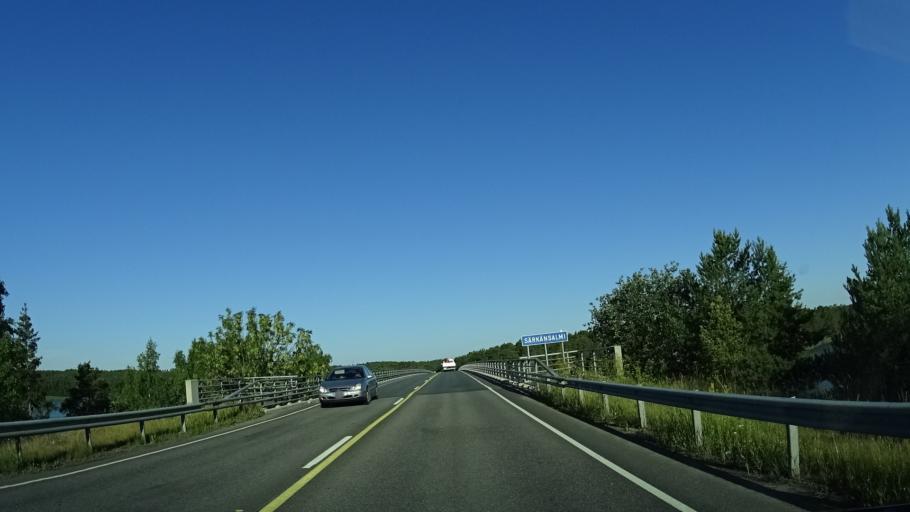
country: FI
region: Varsinais-Suomi
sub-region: Turku
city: Merimasku
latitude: 60.4610
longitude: 21.9303
